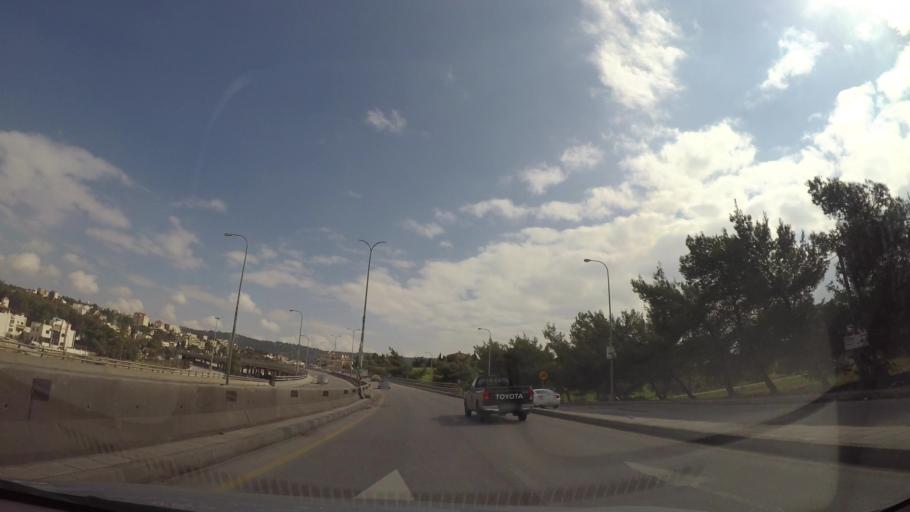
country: JO
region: Amman
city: Al Jubayhah
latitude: 32.0289
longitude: 35.7968
